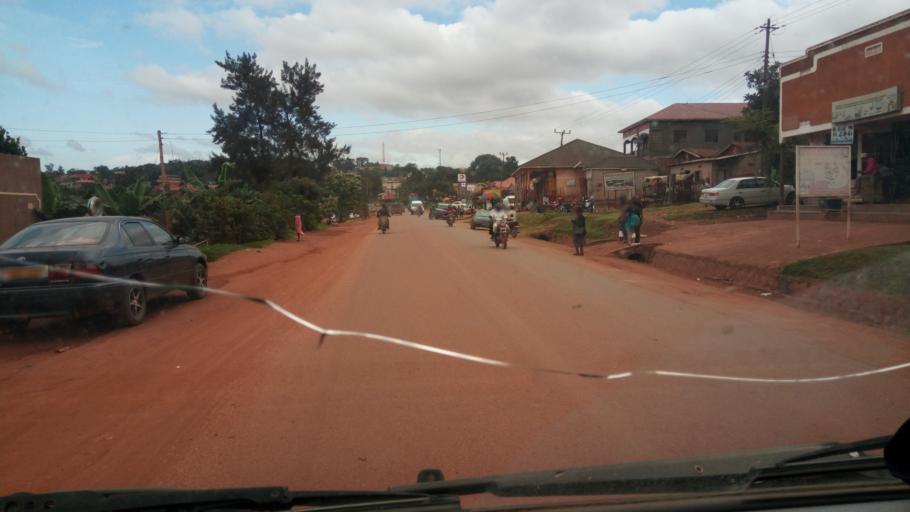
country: UG
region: Central Region
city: Kampala Central Division
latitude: 0.3365
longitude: 32.5481
